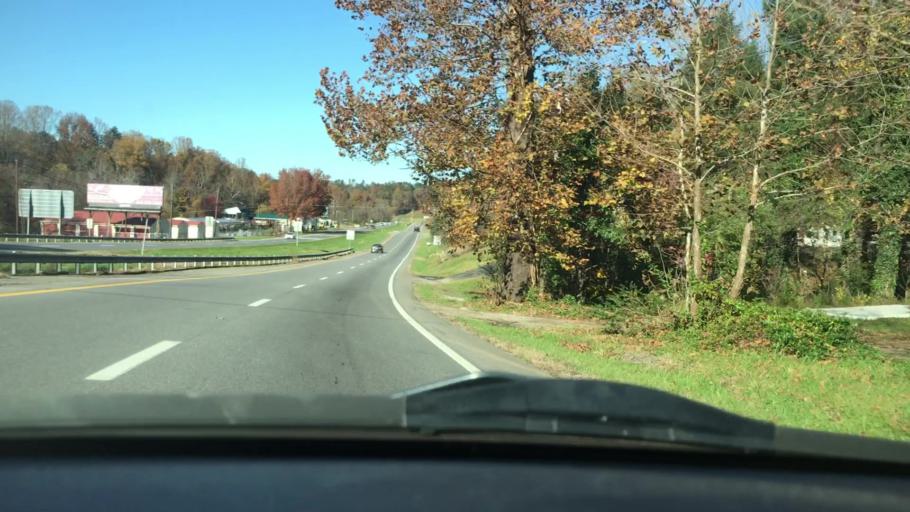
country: US
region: Virginia
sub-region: Henry County
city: Stanleytown
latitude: 36.7516
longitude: -79.9386
